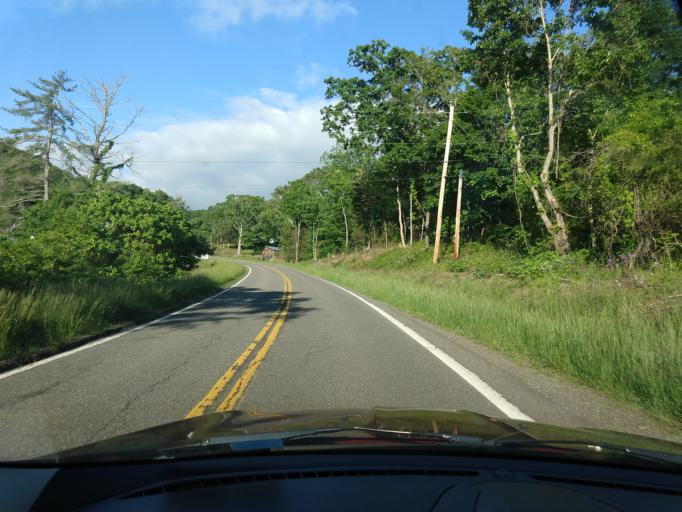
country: US
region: Virginia
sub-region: City of Galax
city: Galax
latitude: 36.8172
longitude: -80.9634
